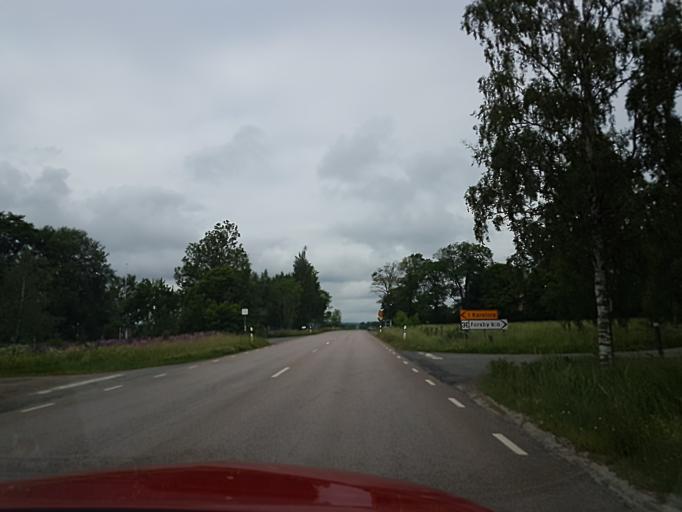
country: SE
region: Vaestra Goetaland
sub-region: Skovde Kommun
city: Skoevde
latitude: 58.3885
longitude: 13.9370
